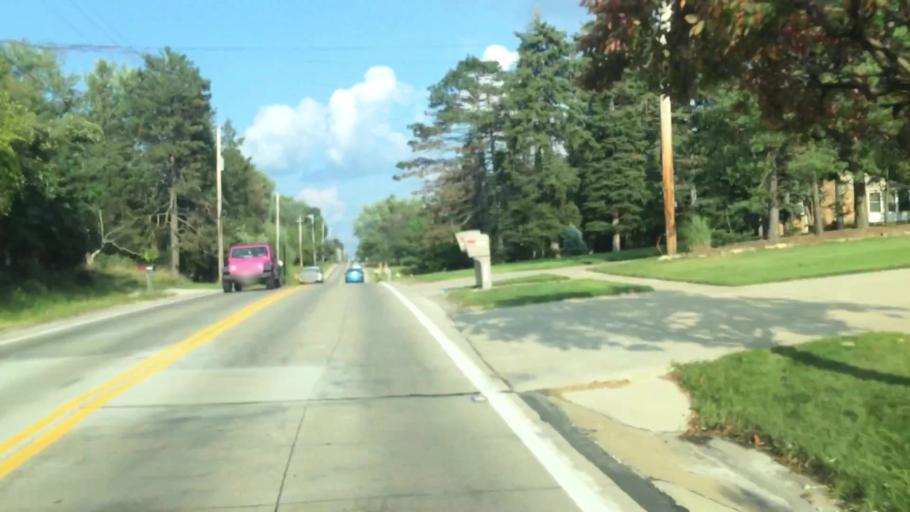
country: US
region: Ohio
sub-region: Cuyahoga County
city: North Royalton
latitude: 41.3510
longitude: -81.7101
